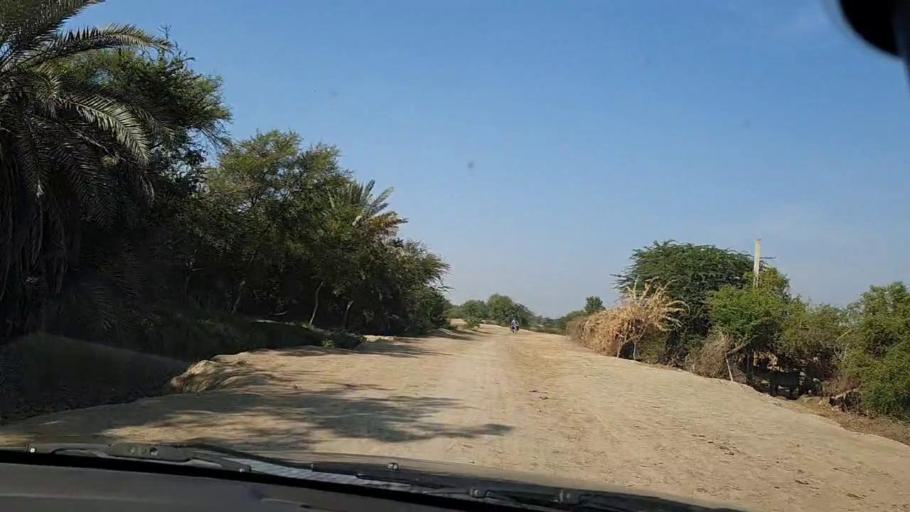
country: PK
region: Sindh
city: Mirpur Batoro
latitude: 24.6527
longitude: 68.2543
